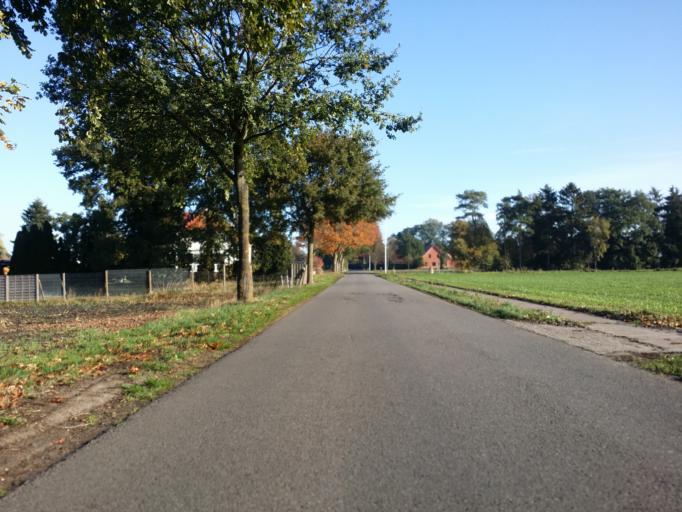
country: DE
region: Lower Saxony
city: Grasberg
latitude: 53.1887
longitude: 9.0164
